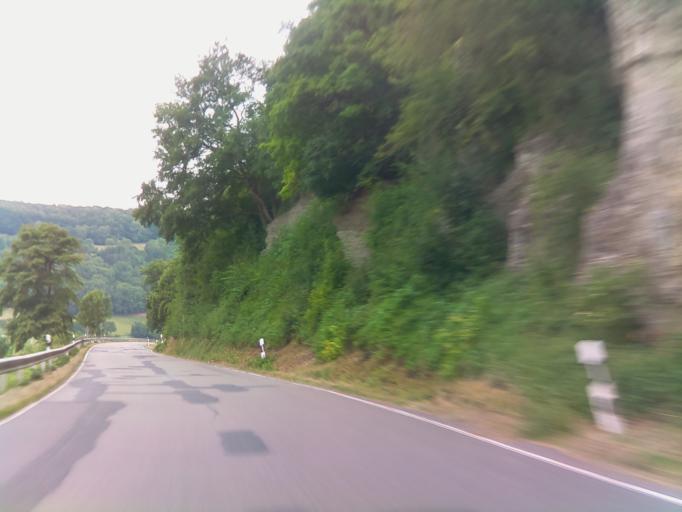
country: DE
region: Lower Saxony
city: Pegestorf
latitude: 51.9188
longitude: 9.4630
